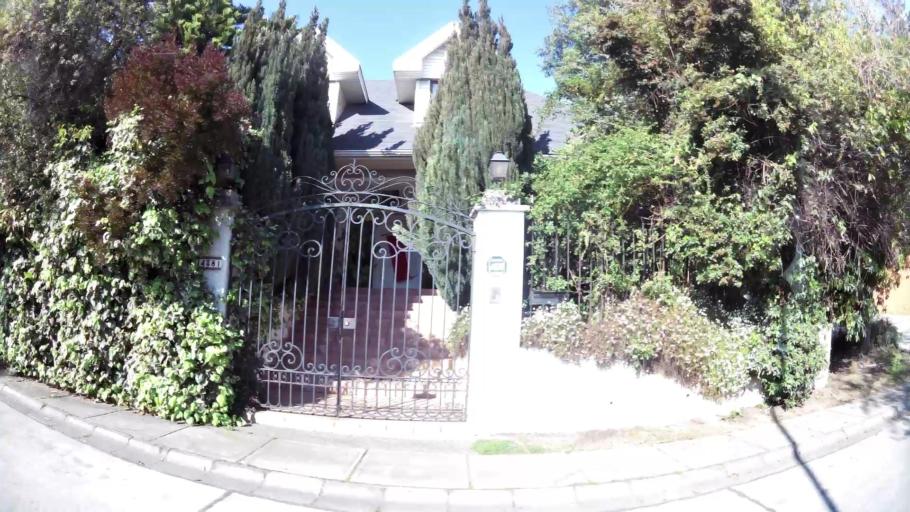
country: CL
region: Santiago Metropolitan
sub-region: Provincia de Santiago
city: Villa Presidente Frei, Nunoa, Santiago, Chile
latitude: -33.3691
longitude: -70.4982
